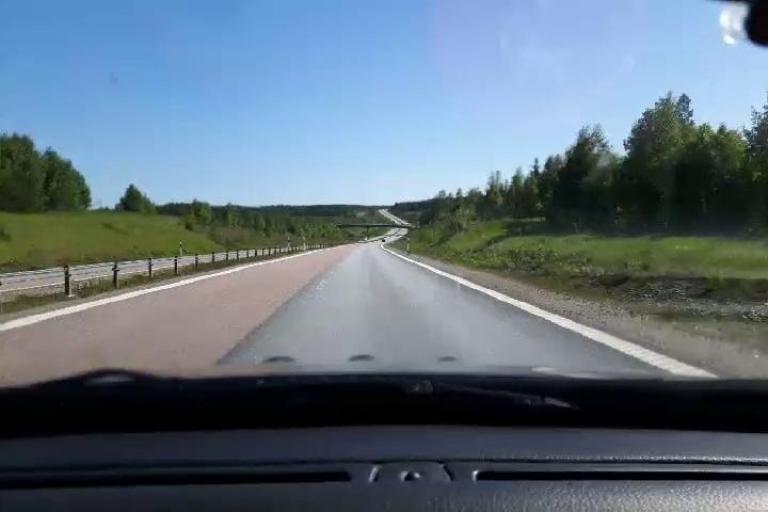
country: SE
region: Gaevleborg
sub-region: Soderhamns Kommun
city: Soderhamn
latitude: 61.3622
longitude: 17.0132
